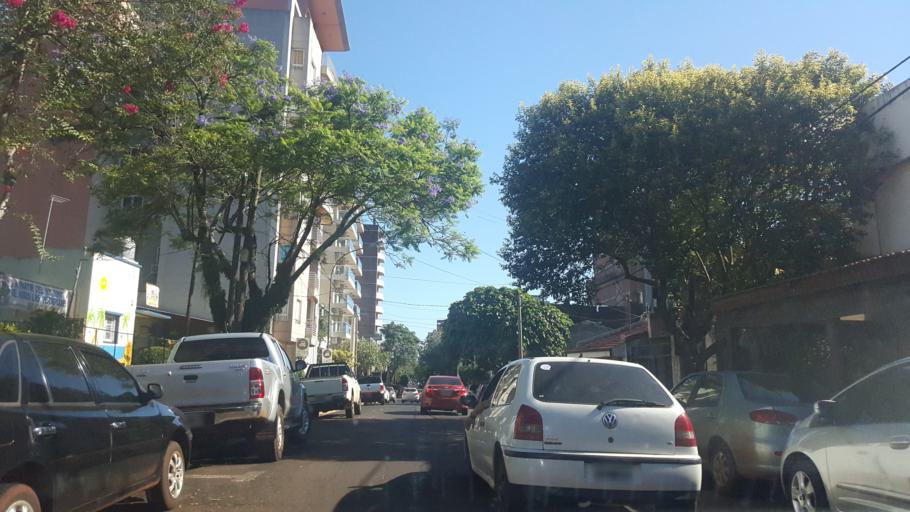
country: AR
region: Misiones
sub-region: Departamento de Capital
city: Posadas
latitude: -27.3729
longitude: -55.8997
